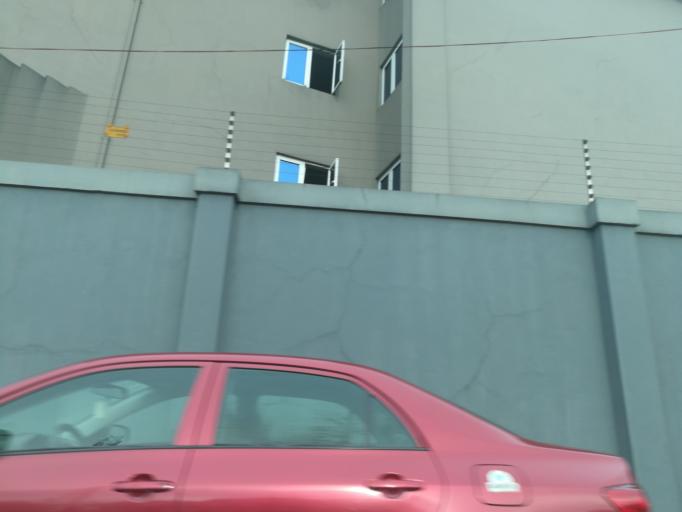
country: NG
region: Rivers
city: Port Harcourt
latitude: 4.8093
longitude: 6.9995
